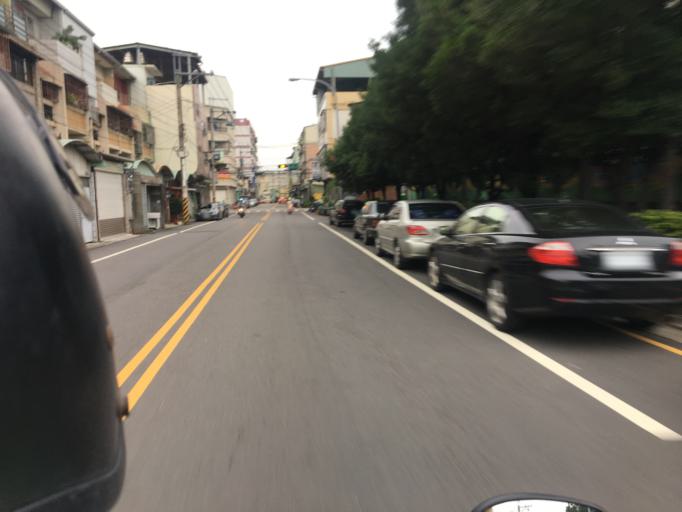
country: TW
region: Taiwan
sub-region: Taichung City
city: Taichung
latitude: 24.0930
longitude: 120.7002
